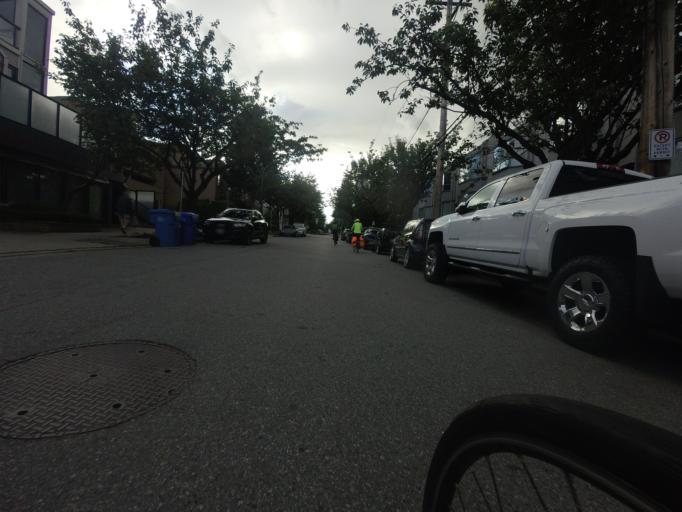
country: CA
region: British Columbia
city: Vancouver
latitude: 49.2651
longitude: -123.1253
